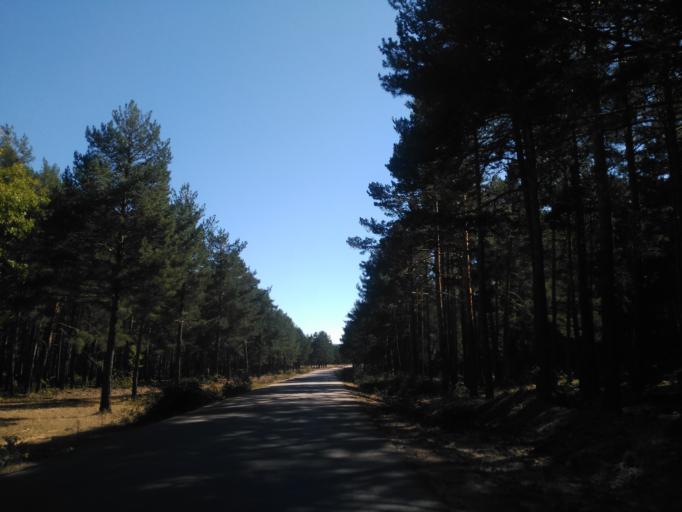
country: ES
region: Castille and Leon
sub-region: Provincia de Soria
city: Vinuesa
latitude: 41.9615
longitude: -2.7865
